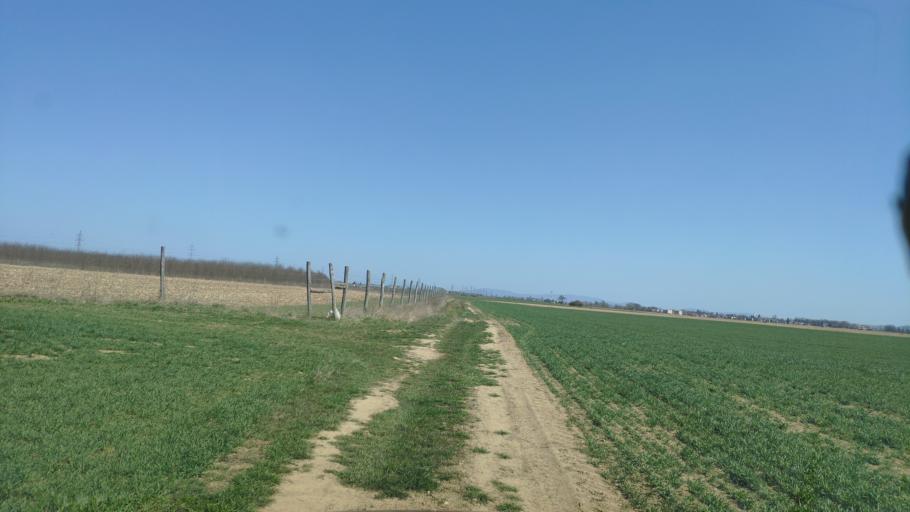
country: SK
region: Kosicky
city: Moldava nad Bodvou
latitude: 48.5936
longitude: 20.9637
